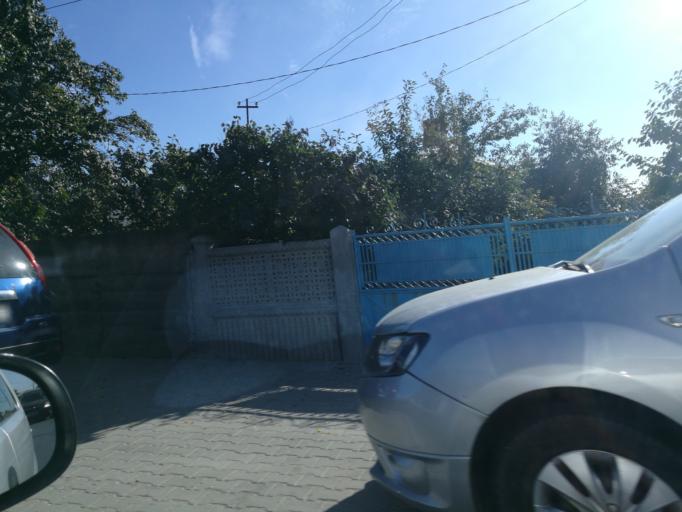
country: RO
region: Ilfov
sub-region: Comuna Dragomiresti-Vale
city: Dragomiresti-Deal
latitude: 44.4559
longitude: 25.9528
